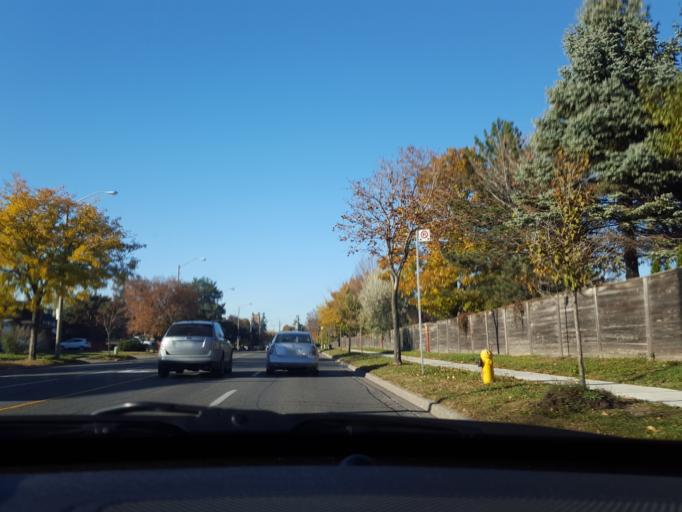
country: CA
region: Ontario
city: Markham
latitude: 43.8251
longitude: -79.2860
